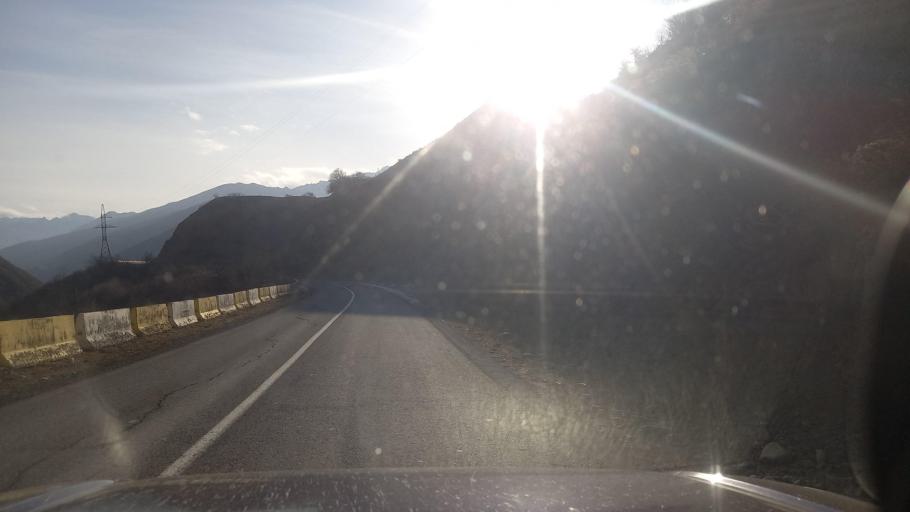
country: RU
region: Ingushetiya
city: Dzhayrakh
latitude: 42.8330
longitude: 44.6637
